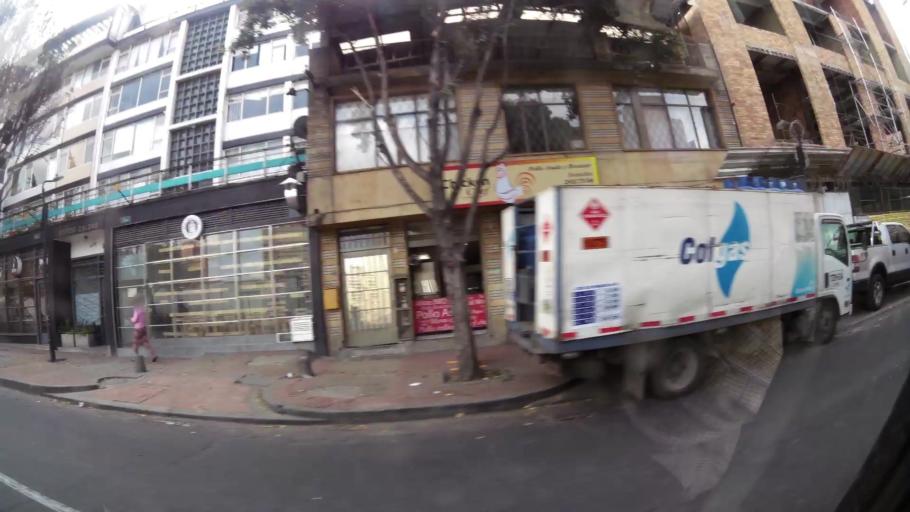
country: CO
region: Bogota D.C.
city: Bogota
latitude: 4.6141
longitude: -74.0669
